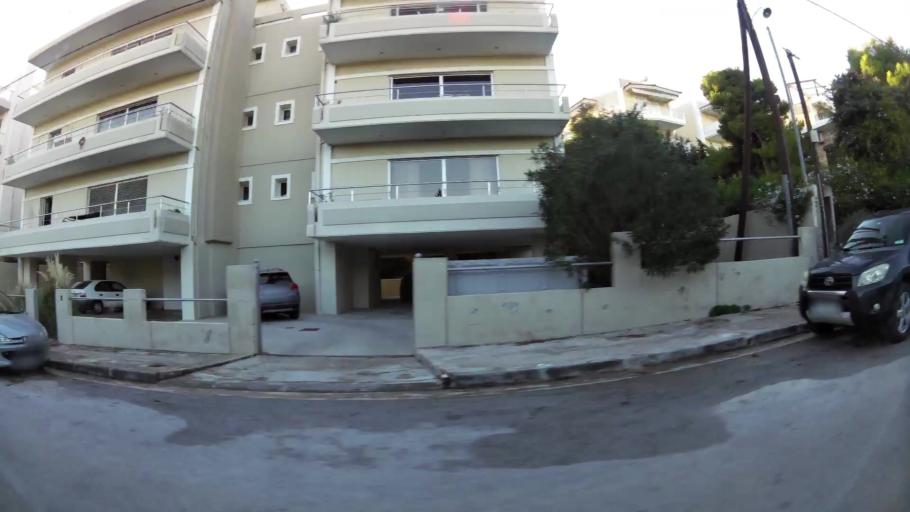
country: GR
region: Attica
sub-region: Nomarchia Anatolikis Attikis
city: Rafina
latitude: 38.0092
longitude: 24.0180
